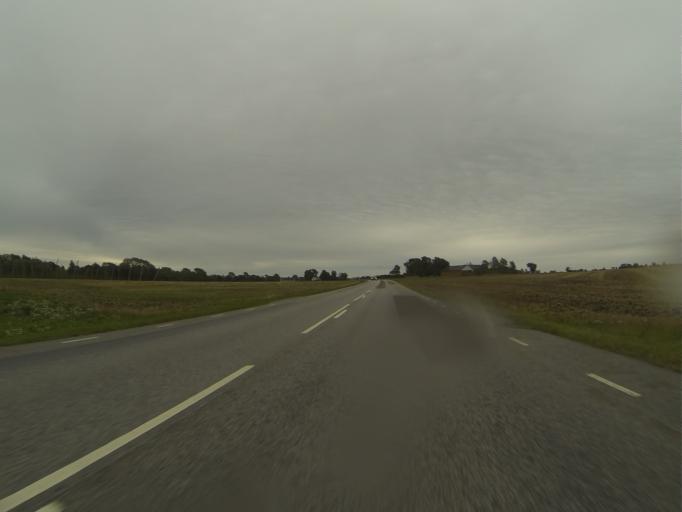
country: SE
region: Skane
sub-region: Svedala Kommun
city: Klagerup
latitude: 55.6352
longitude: 13.2836
